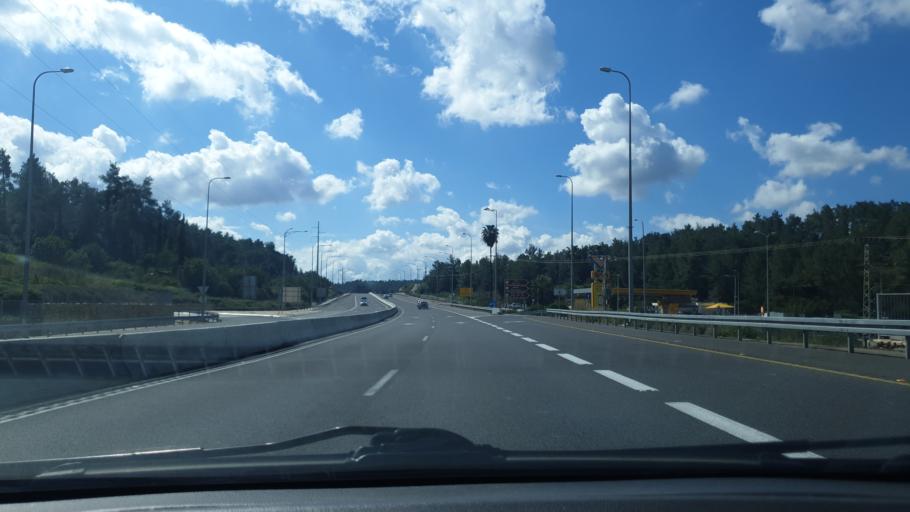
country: IL
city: Mevo horon
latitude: 31.8092
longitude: 35.0189
